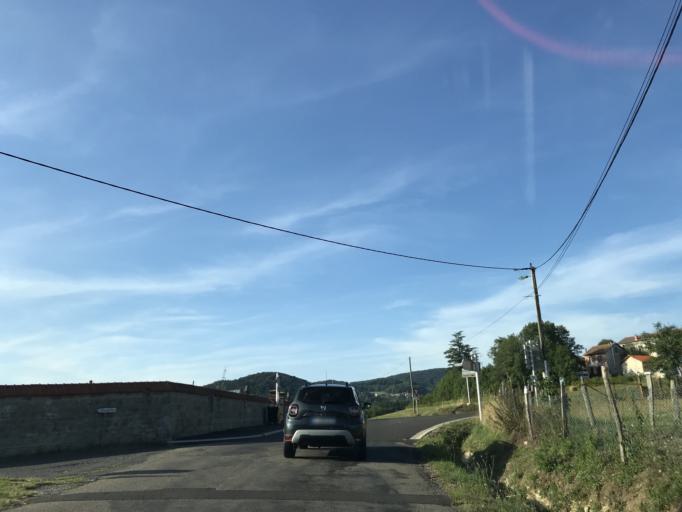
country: FR
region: Auvergne
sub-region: Departement du Puy-de-Dome
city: Job
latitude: 45.7106
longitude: 3.7166
